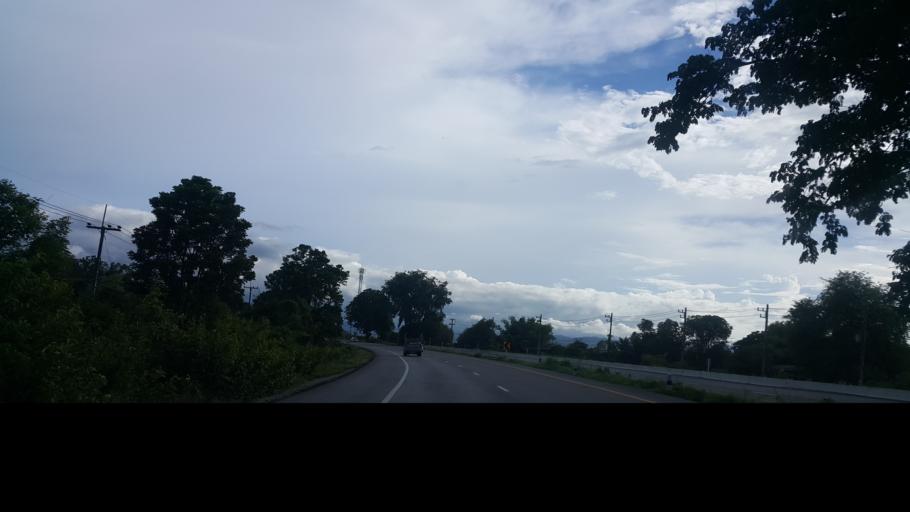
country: TH
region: Tak
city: Ban Tak
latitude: 17.1069
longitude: 99.0768
